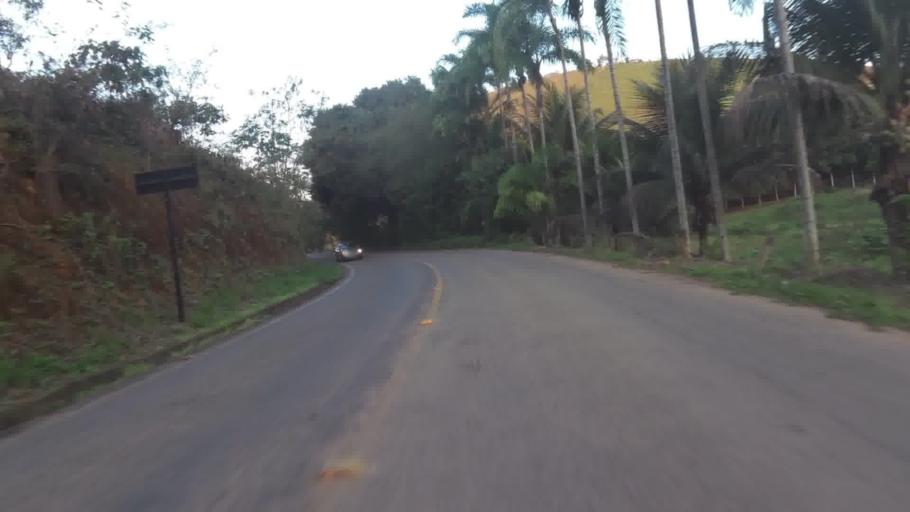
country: BR
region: Espirito Santo
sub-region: Alfredo Chaves
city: Alfredo Chaves
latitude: -20.6477
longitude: -40.6623
